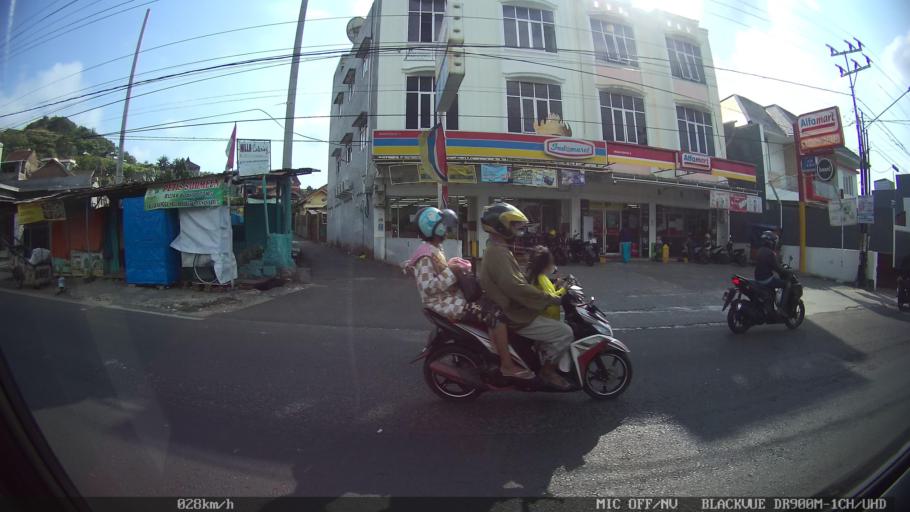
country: ID
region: Lampung
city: Bandarlampung
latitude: -5.4067
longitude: 105.2535
